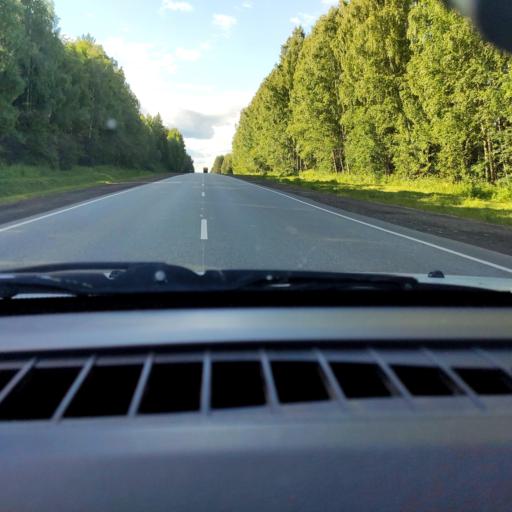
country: RU
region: Perm
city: Kungur
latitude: 57.4371
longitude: 56.8219
